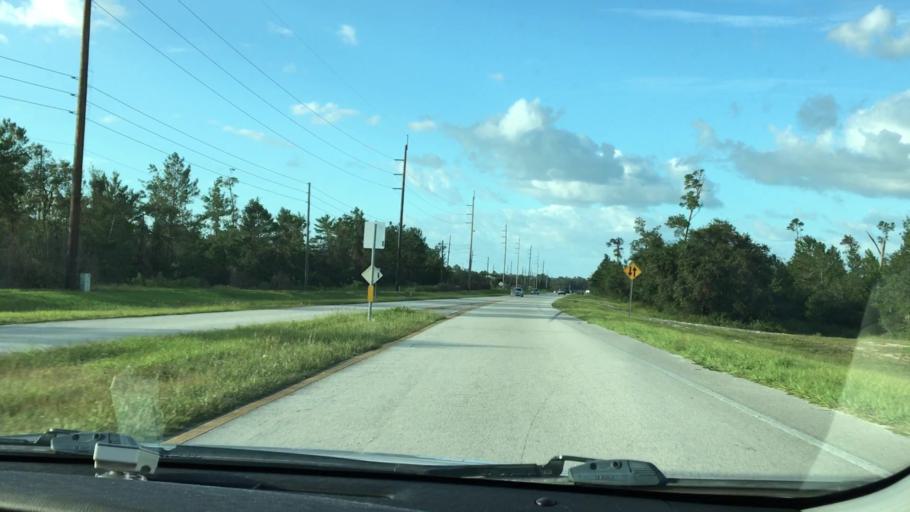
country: US
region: Florida
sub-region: Volusia County
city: Deltona
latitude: 28.9224
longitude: -81.2818
